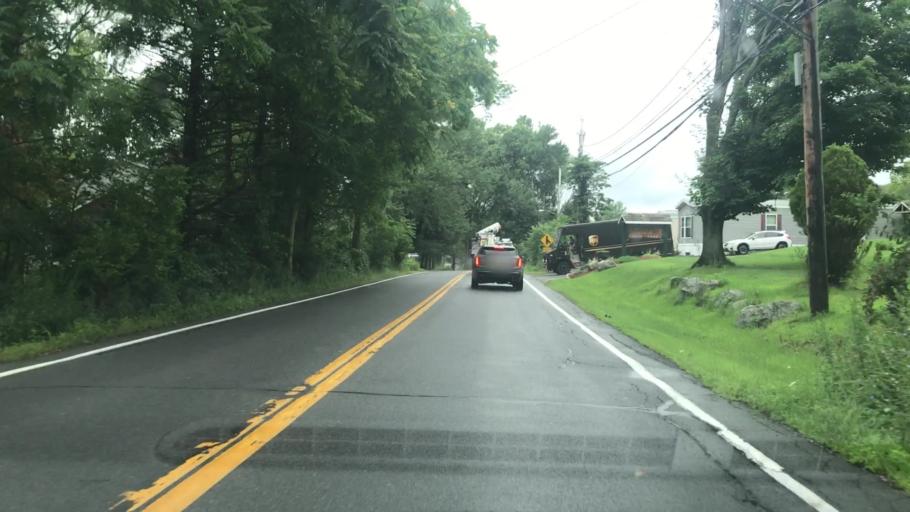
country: US
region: New York
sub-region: Westchester County
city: Jefferson Valley-Yorktown
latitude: 41.3470
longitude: -73.7833
